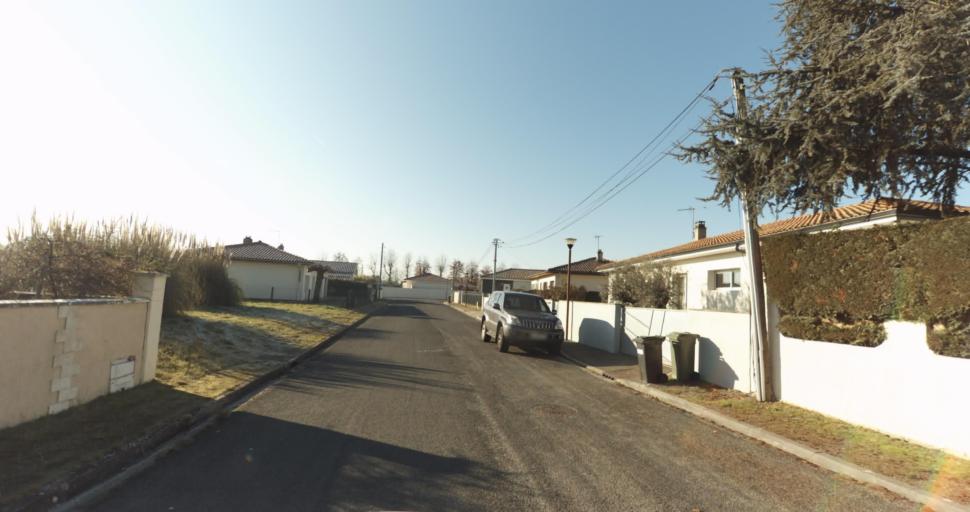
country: FR
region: Aquitaine
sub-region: Departement de la Gironde
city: Bassens
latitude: 44.8896
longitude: -0.5139
